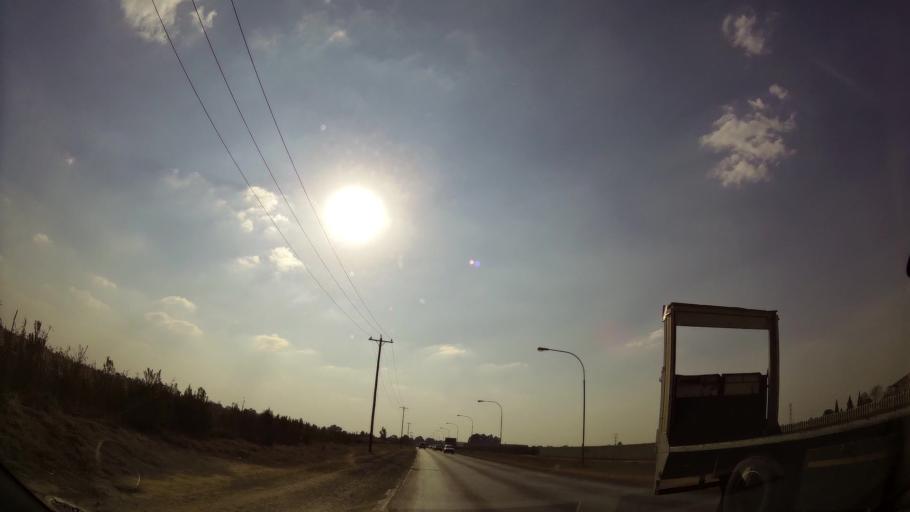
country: ZA
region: Gauteng
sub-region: Ekurhuleni Metropolitan Municipality
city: Benoni
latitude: -26.1439
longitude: 28.3945
